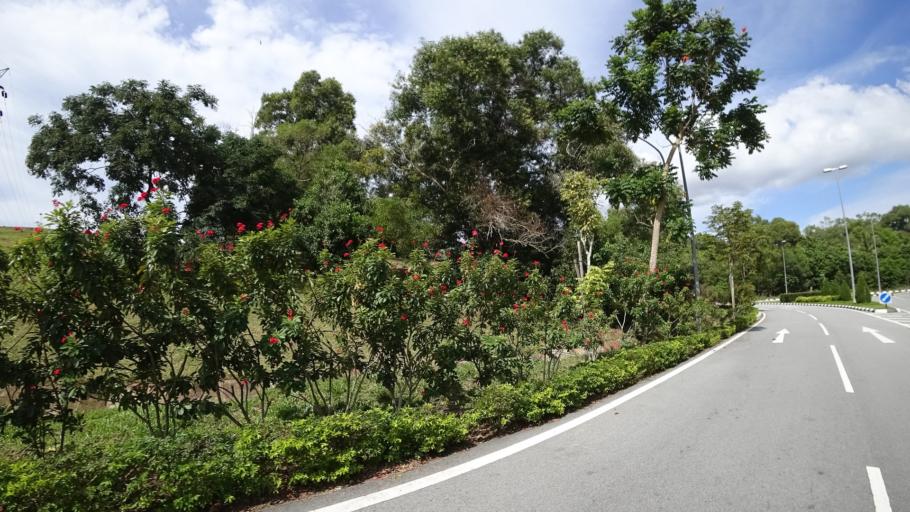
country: BN
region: Brunei and Muara
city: Bandar Seri Begawan
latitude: 4.9424
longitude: 114.9354
